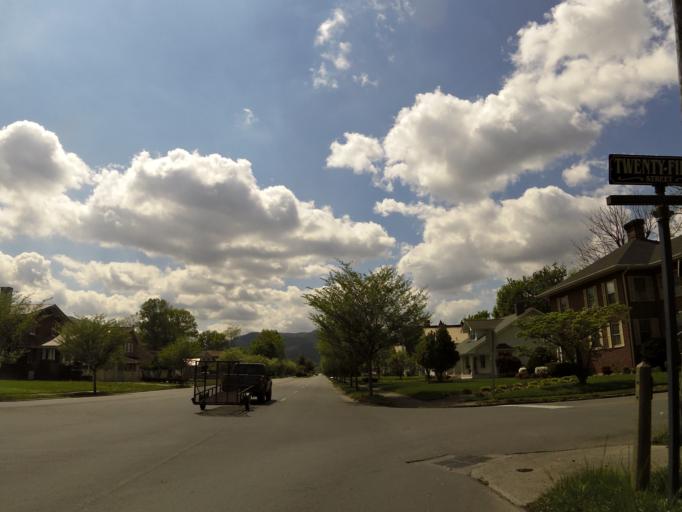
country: US
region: Kentucky
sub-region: Bell County
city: Middlesboro
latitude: 36.6067
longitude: -83.7218
